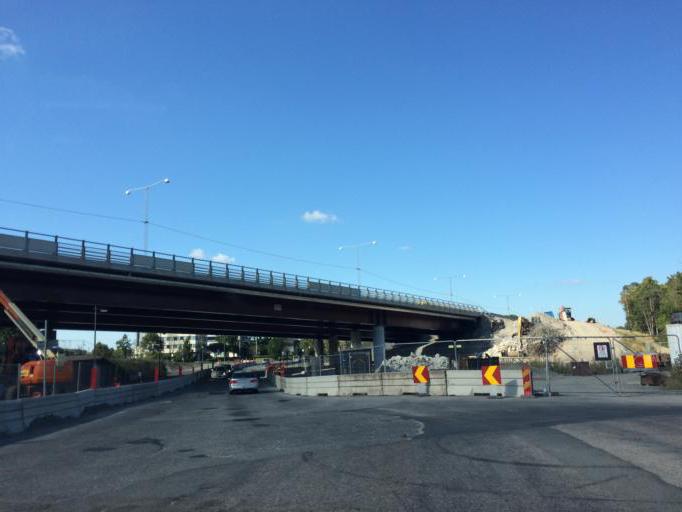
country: SE
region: Stockholm
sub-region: Upplands Vasby Kommun
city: Upplands Vaesby
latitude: 59.4743
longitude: 17.9177
